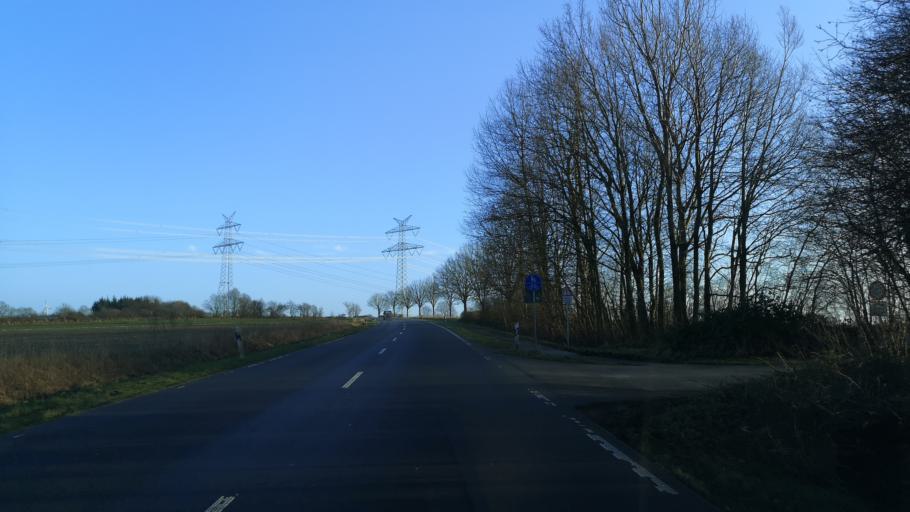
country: DE
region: Schleswig-Holstein
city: Tarp
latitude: 54.6662
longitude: 9.4152
